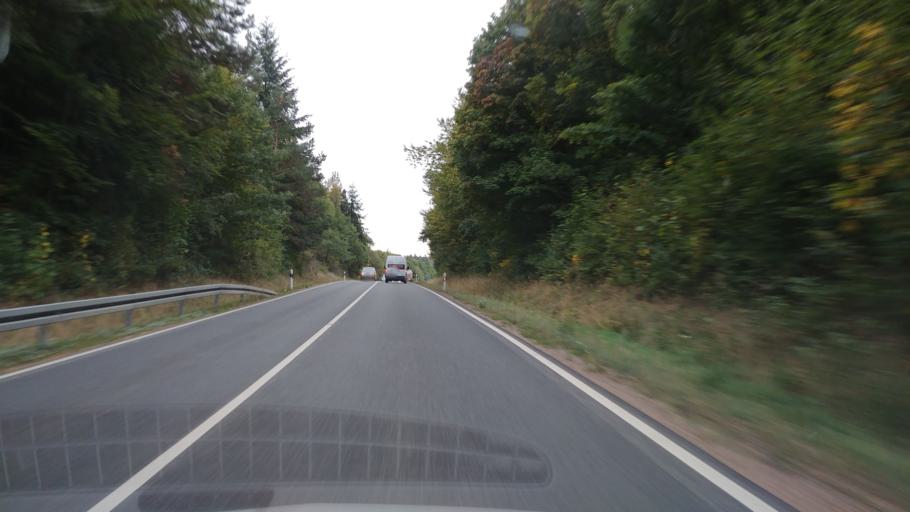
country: DE
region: Rheinland-Pfalz
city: Kaltenholzhausen
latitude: 50.2719
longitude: 8.1689
